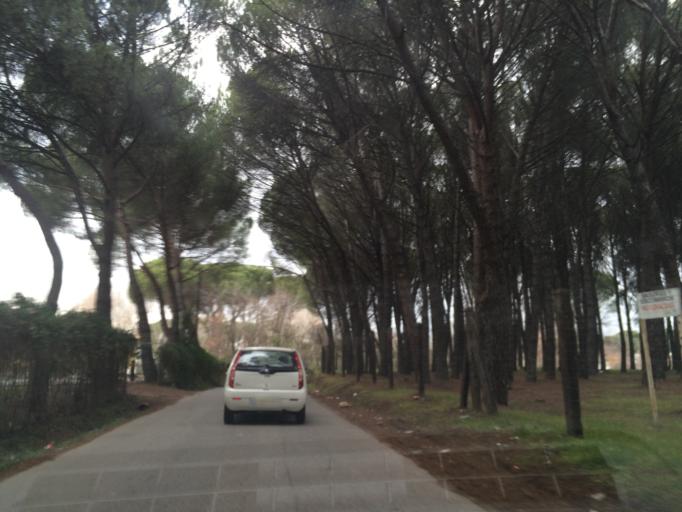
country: ES
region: Madrid
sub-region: Provincia de Madrid
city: Arroyomolinos
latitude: 40.2992
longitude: -3.9435
